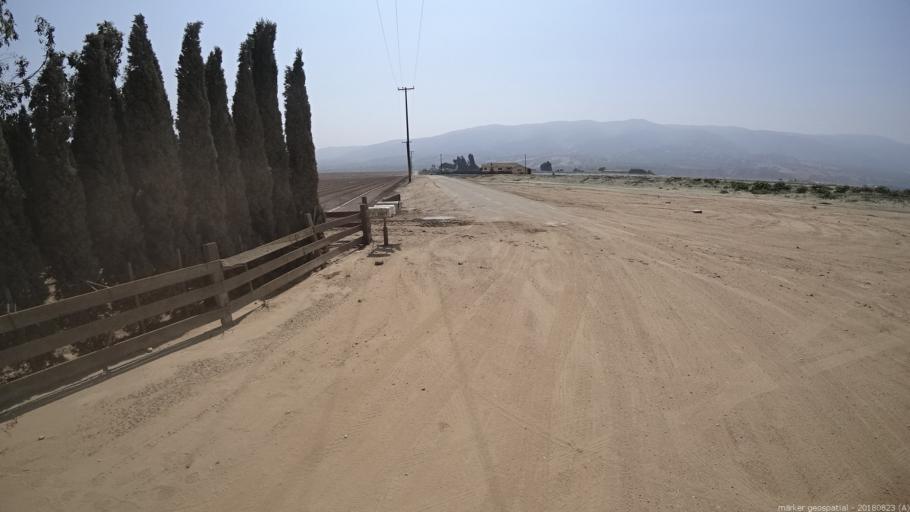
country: US
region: California
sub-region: Monterey County
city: Soledad
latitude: 36.4094
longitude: -121.3476
